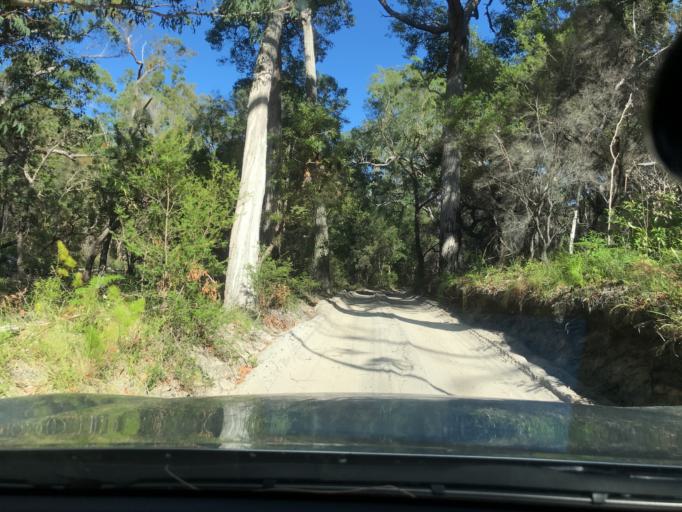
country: AU
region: Queensland
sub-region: Fraser Coast
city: Urangan
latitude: -25.5000
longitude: 153.1040
